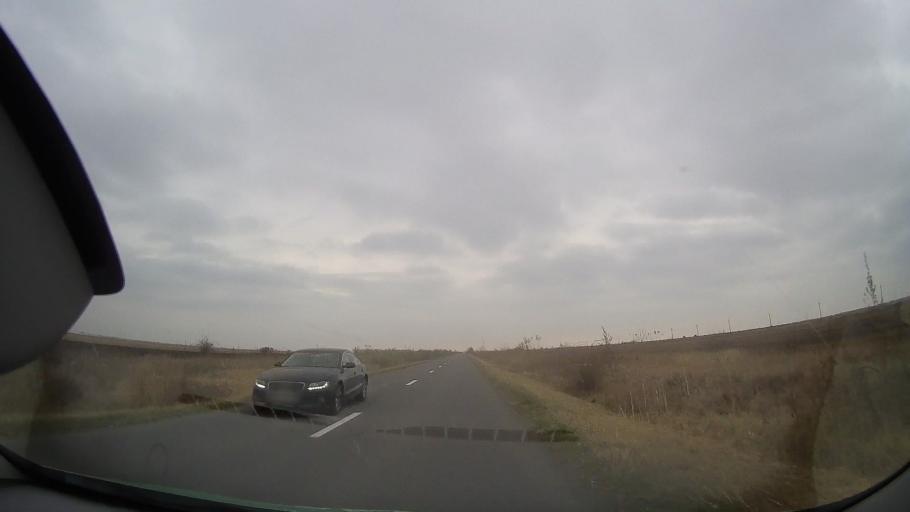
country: RO
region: Ialomita
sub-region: Comuna Garbovi
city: Garbovi
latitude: 44.7544
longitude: 26.7250
